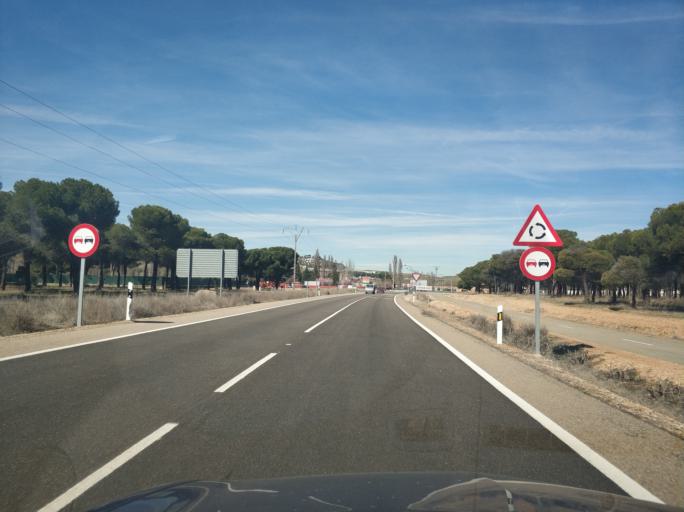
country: ES
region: Castille and Leon
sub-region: Provincia de Valladolid
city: Simancas
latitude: 41.5796
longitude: -4.8137
